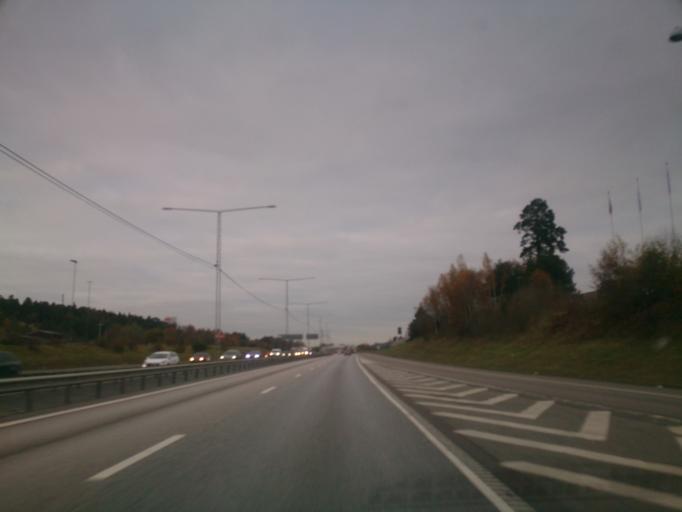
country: SE
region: Stockholm
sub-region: Upplands Vasby Kommun
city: Upplands Vaesby
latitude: 59.5174
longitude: 17.9253
